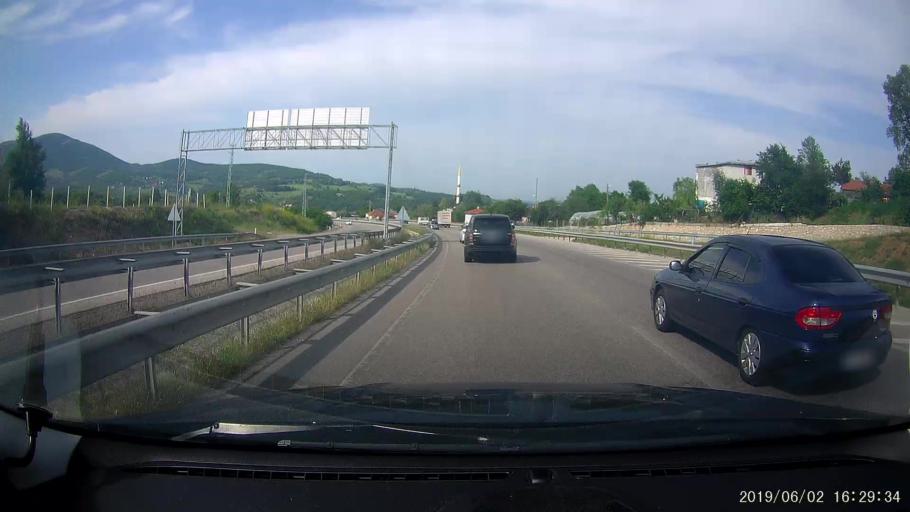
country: TR
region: Samsun
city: Ladik
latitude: 41.0143
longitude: 35.8709
